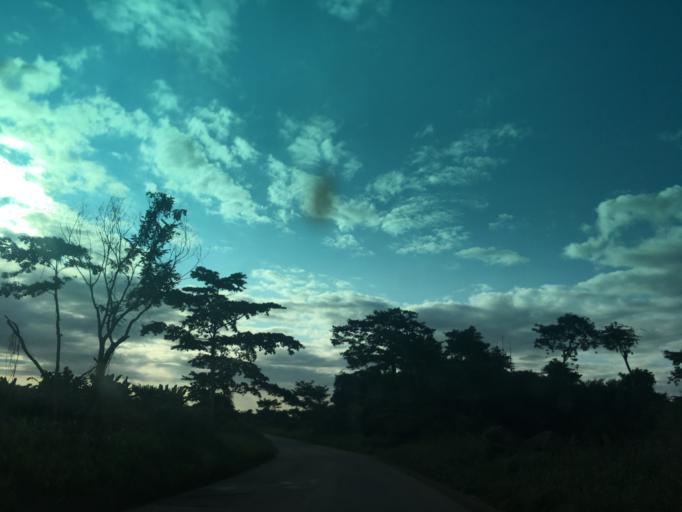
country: GH
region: Western
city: Bibiani
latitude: 6.2959
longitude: -2.2374
